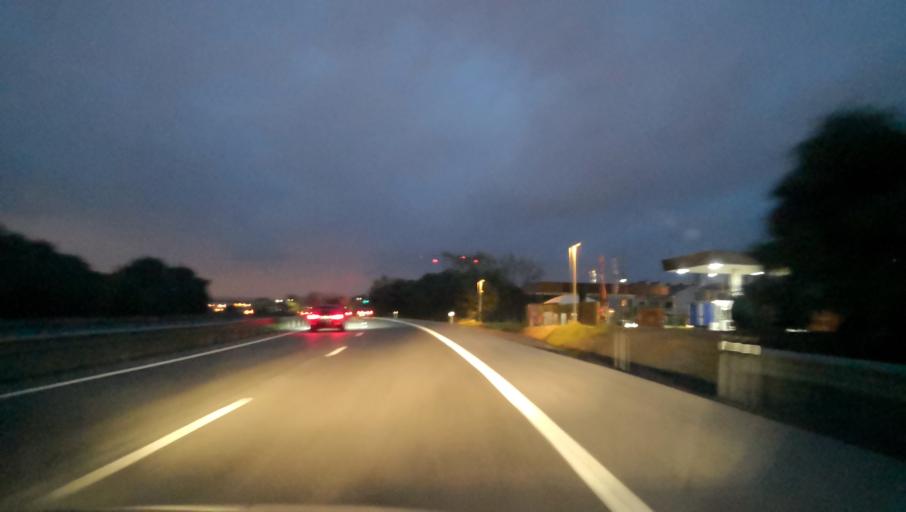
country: PT
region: Setubal
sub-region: Barreiro
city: Santo Antonio da Charneca
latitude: 38.6356
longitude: -9.0445
